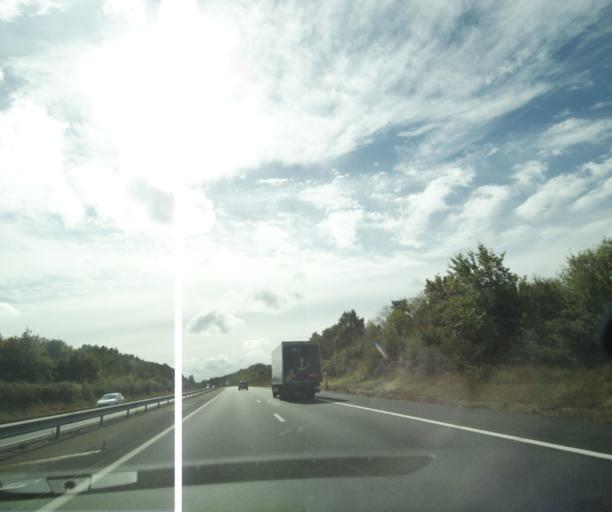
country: FR
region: Poitou-Charentes
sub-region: Departement de la Charente-Maritime
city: Thenac
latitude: 45.6453
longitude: -0.6301
